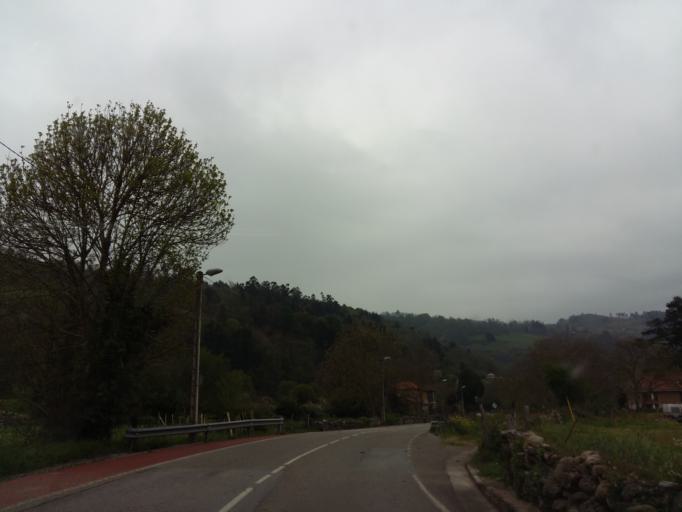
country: ES
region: Cantabria
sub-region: Provincia de Cantabria
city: Arenas de Iguna
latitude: 43.1949
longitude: -4.0630
